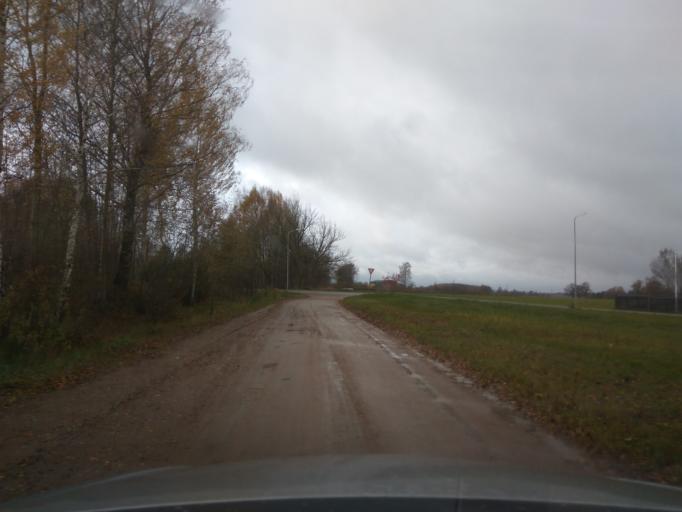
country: LV
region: Kuldigas Rajons
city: Kuldiga
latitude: 56.9702
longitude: 21.9377
